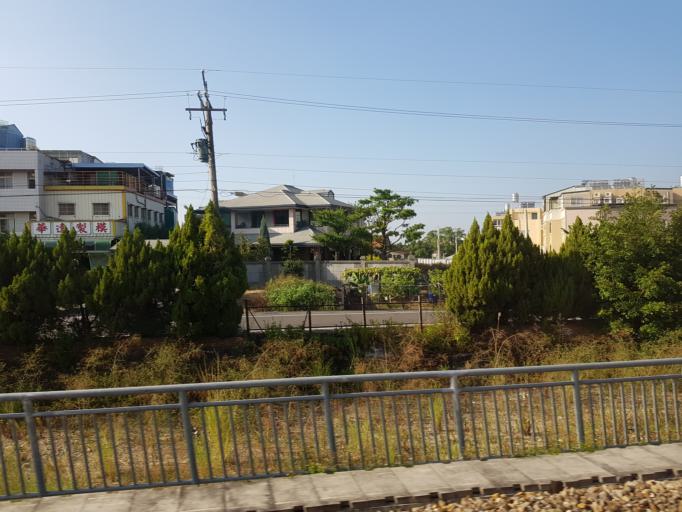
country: TW
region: Taiwan
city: Fengyuan
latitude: 24.2612
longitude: 120.7300
